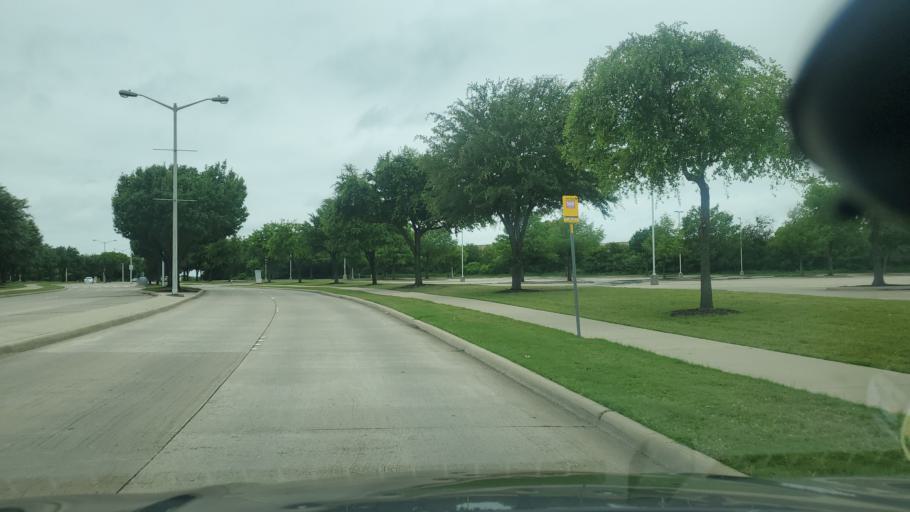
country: US
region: Texas
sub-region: Dallas County
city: Garland
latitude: 32.9607
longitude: -96.6412
